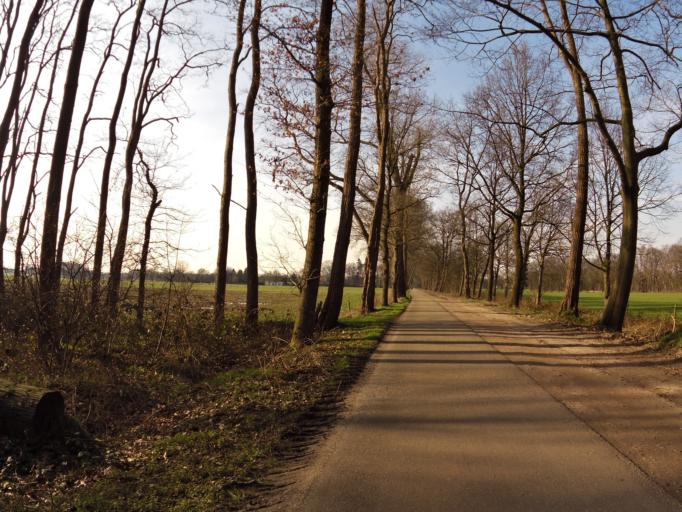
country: NL
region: North Brabant
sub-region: Gemeente Vught
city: Vught
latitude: 51.6292
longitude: 5.2577
